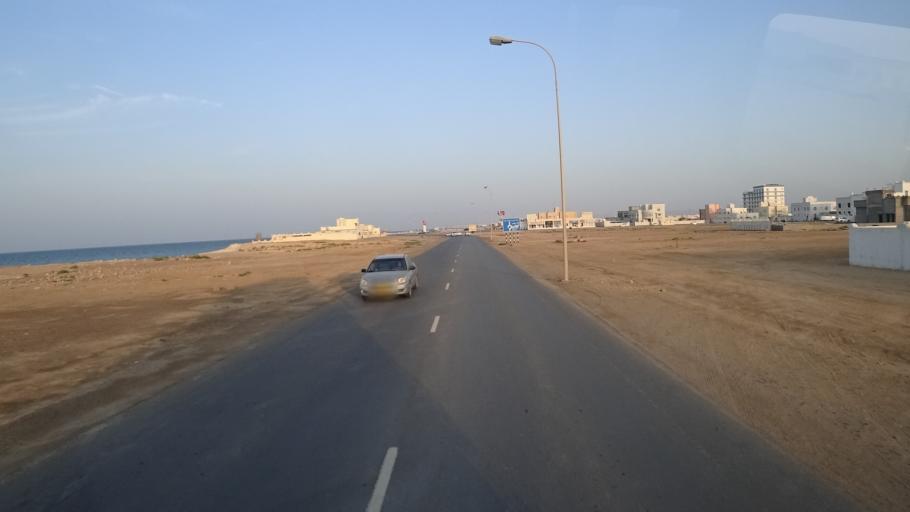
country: OM
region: Ash Sharqiyah
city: Sur
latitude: 22.6048
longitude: 59.4788
